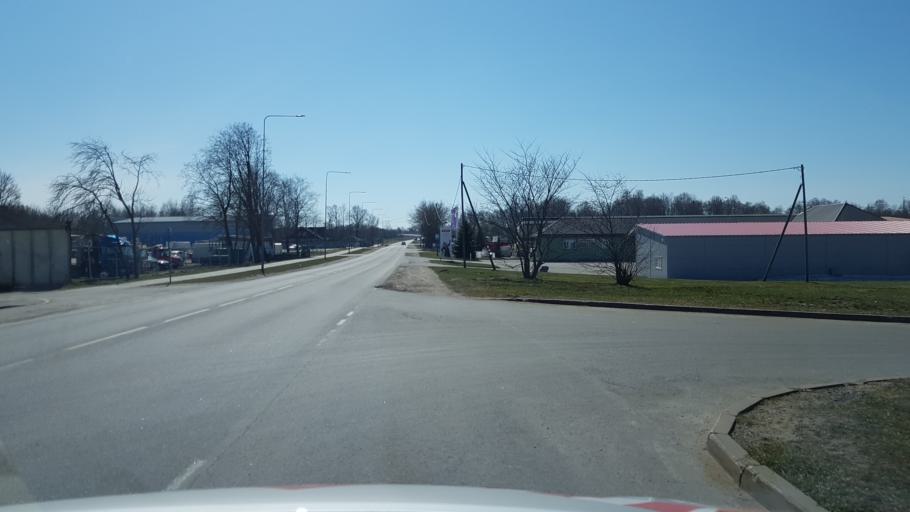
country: EE
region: Ida-Virumaa
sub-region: Johvi vald
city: Johvi
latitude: 59.3511
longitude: 27.4087
